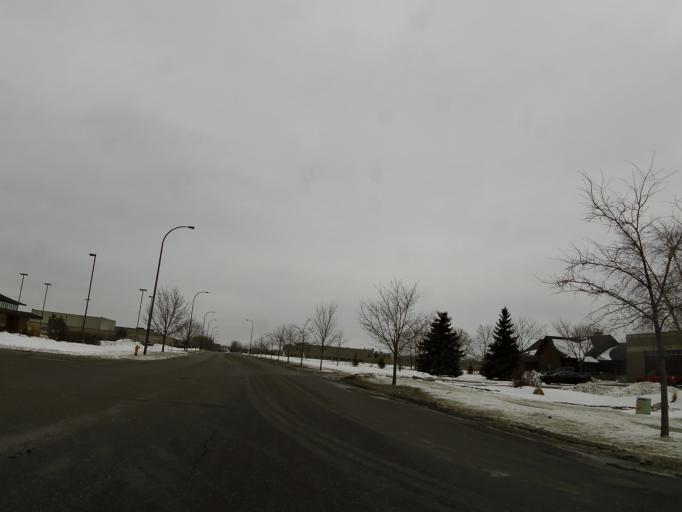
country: US
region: Minnesota
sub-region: Dakota County
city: South Saint Paul
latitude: 44.8877
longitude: -93.0237
